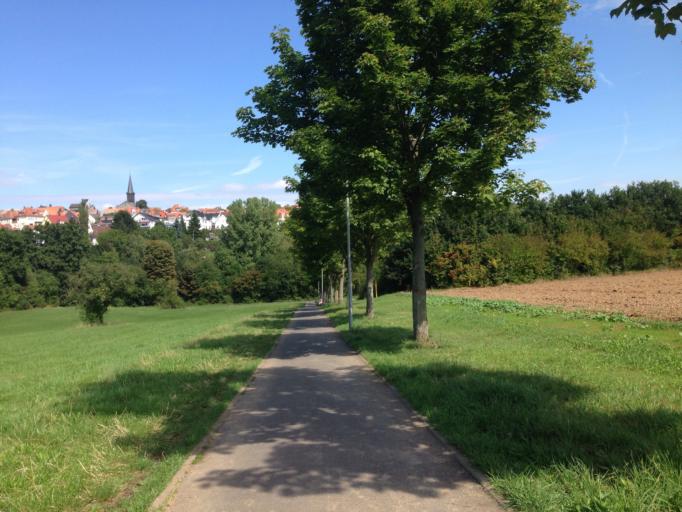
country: DE
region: Hesse
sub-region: Regierungsbezirk Giessen
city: Grunberg
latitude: 50.5855
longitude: 8.9572
